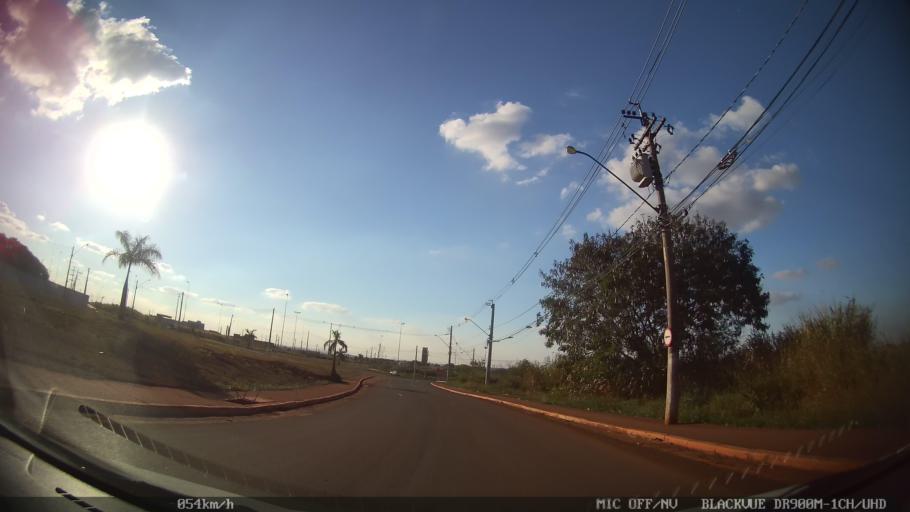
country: BR
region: Sao Paulo
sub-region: Santa Barbara D'Oeste
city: Santa Barbara d'Oeste
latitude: -22.7460
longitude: -47.3979
